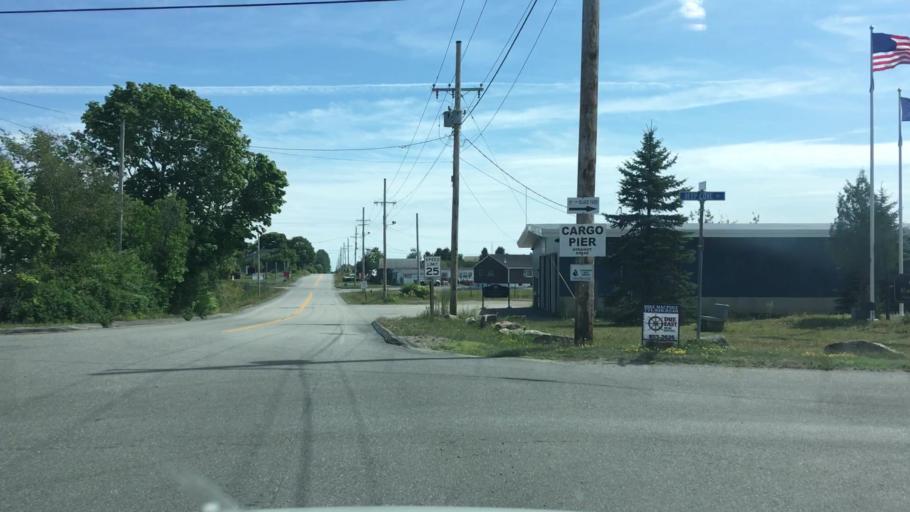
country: US
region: Maine
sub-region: Washington County
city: Eastport
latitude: 44.9067
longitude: -66.9974
